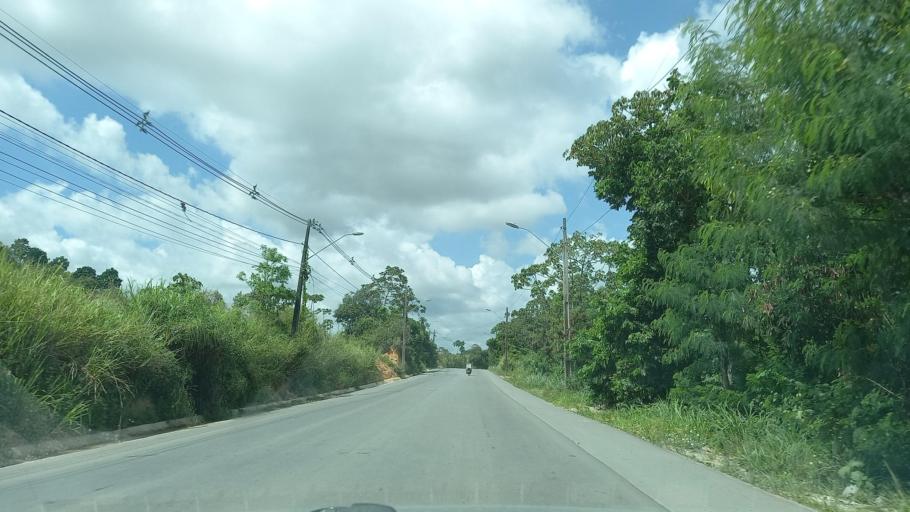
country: BR
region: Pernambuco
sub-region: Jaboatao Dos Guararapes
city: Jaboatao
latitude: -8.1611
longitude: -34.9877
